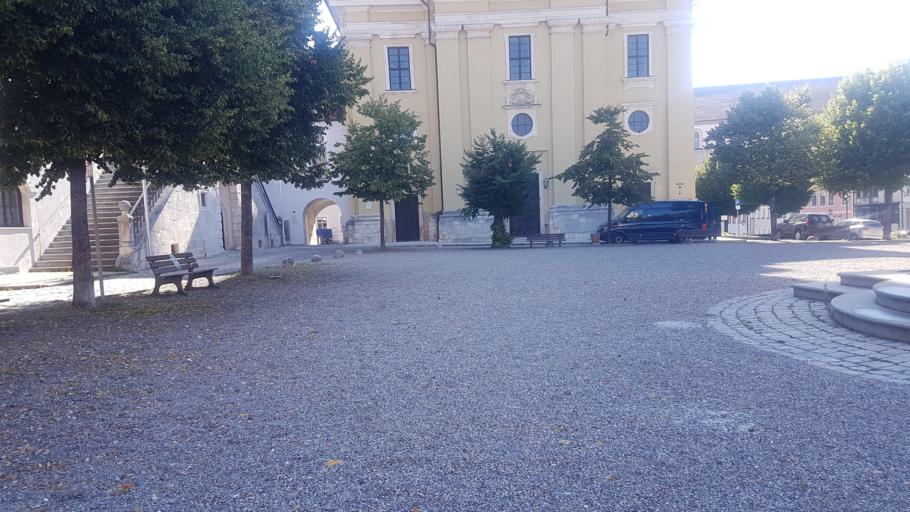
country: DE
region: Bavaria
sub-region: Upper Bavaria
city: Neuburg an der Donau
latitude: 48.7376
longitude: 11.1785
